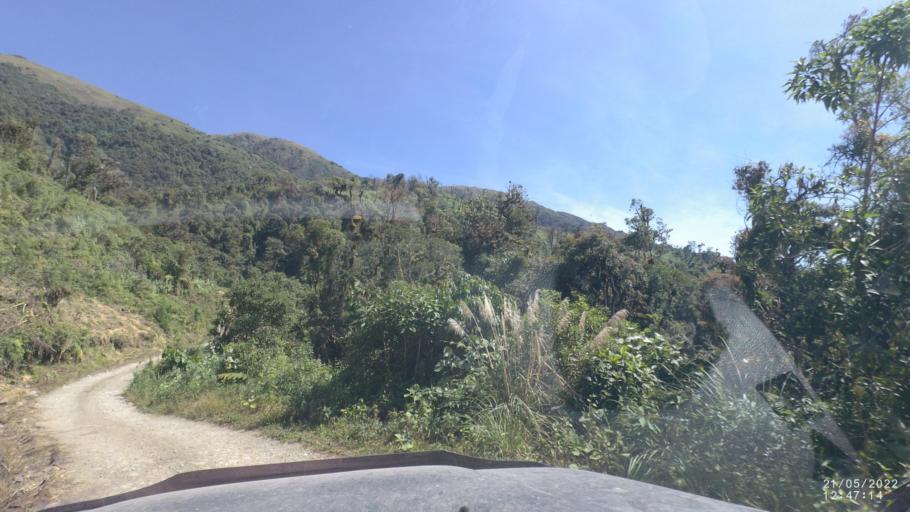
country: BO
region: Cochabamba
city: Colomi
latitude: -17.1826
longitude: -65.9410
